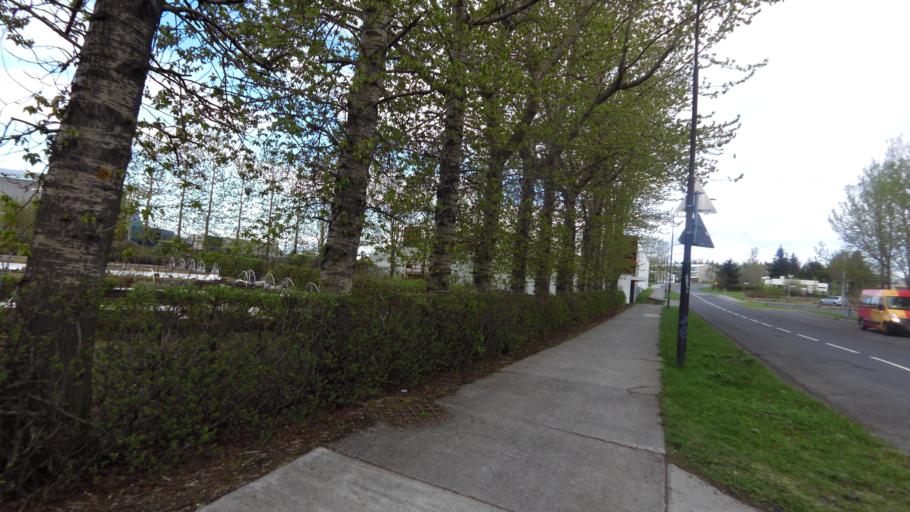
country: IS
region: Capital Region
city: Reykjavik
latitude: 64.1175
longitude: -21.8501
